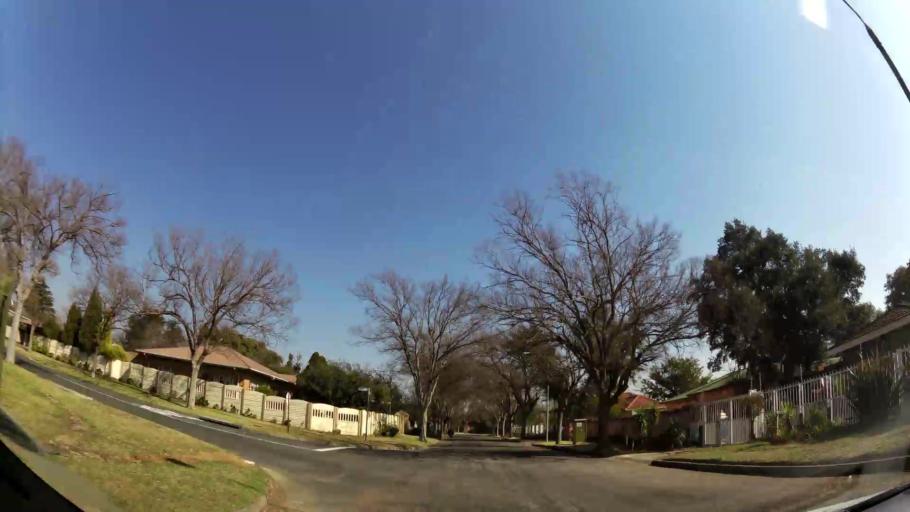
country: ZA
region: Gauteng
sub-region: Ekurhuleni Metropolitan Municipality
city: Boksburg
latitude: -26.2429
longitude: 28.2542
